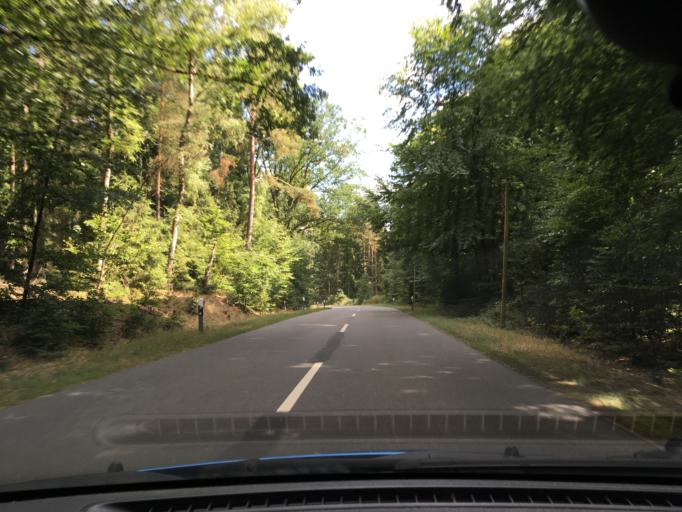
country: DE
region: Lower Saxony
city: Rehlingen
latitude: 53.0779
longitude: 10.2283
